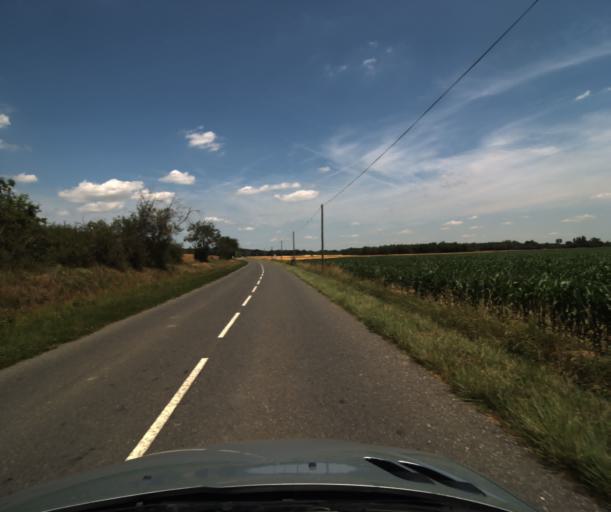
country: FR
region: Midi-Pyrenees
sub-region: Departement de la Haute-Garonne
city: Labastidette
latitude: 43.4817
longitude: 1.2166
